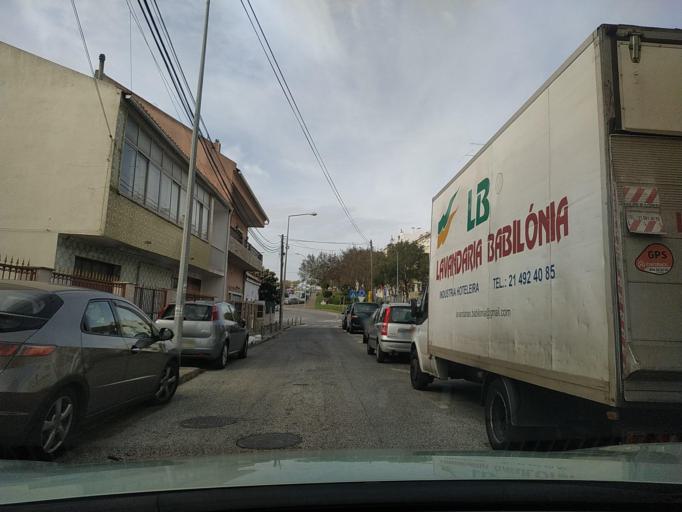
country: PT
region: Lisbon
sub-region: Amadora
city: Amadora
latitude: 38.7775
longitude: -9.2348
